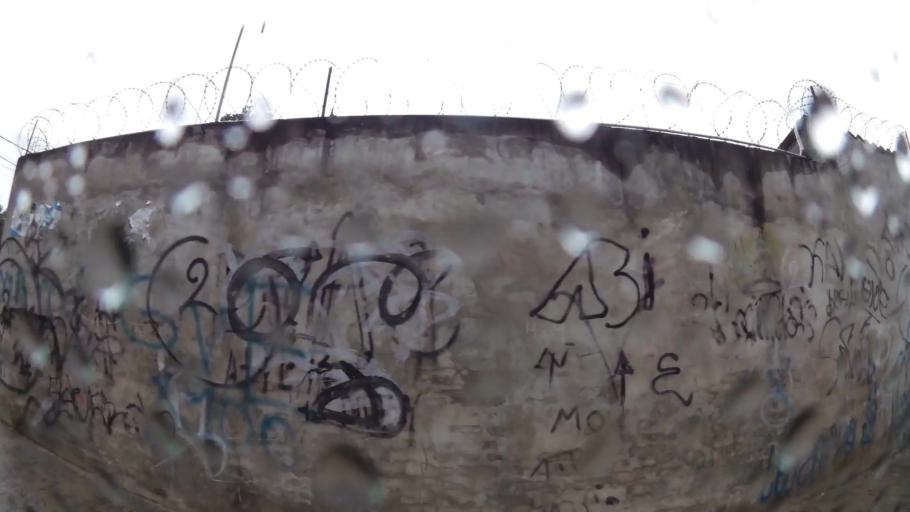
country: BO
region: Santa Cruz
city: Santa Cruz de la Sierra
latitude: -17.7975
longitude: -63.2088
